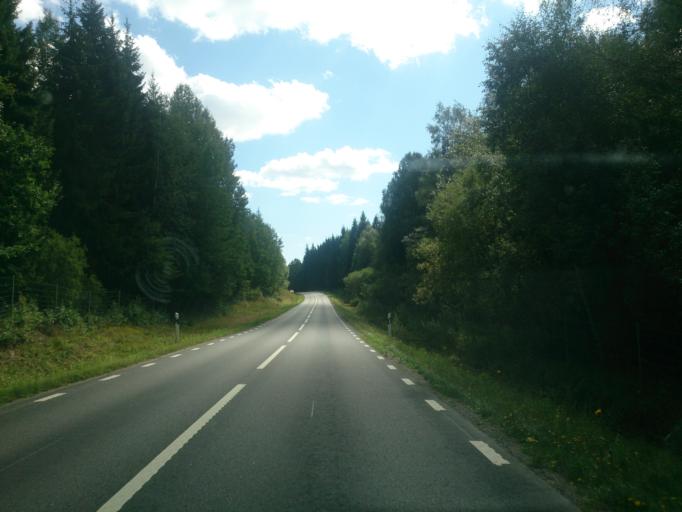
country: SE
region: OEstergoetland
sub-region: Atvidabergs Kommun
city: Atvidaberg
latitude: 58.1756
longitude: 16.0291
